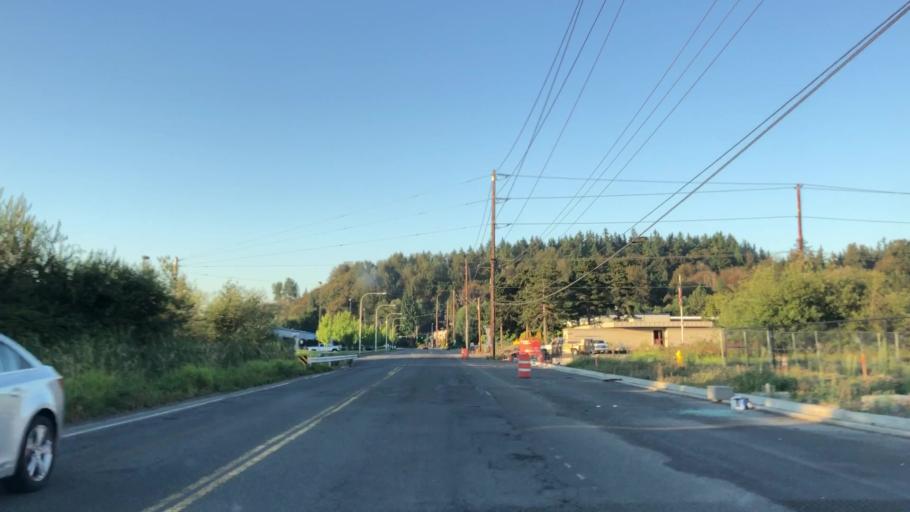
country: US
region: Washington
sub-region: King County
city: Lakeland North
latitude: 47.3441
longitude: -122.2499
